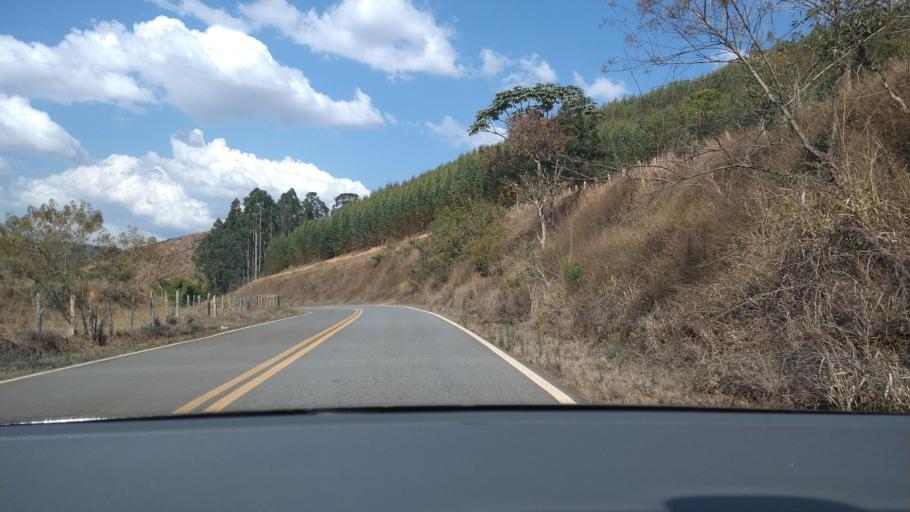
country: BR
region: Minas Gerais
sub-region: Rio Piracicaba
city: Rio Piracicaba
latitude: -19.9680
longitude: -43.1528
